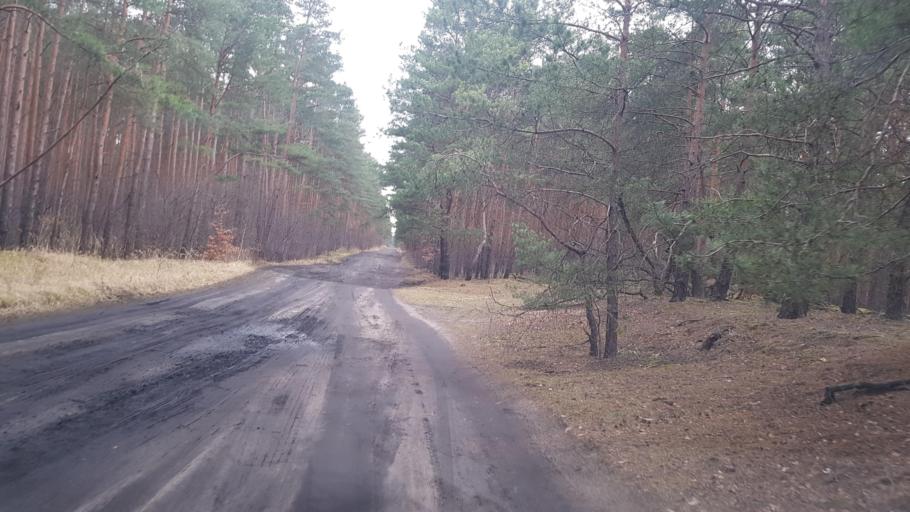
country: DE
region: Brandenburg
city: Halbe
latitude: 52.0636
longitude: 13.6692
